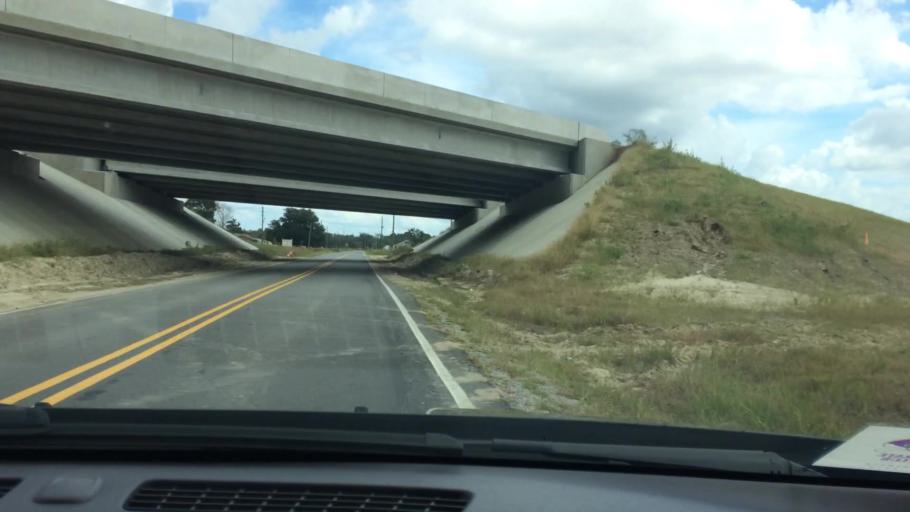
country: US
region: North Carolina
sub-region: Pitt County
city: Ayden
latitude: 35.4670
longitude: -77.4430
